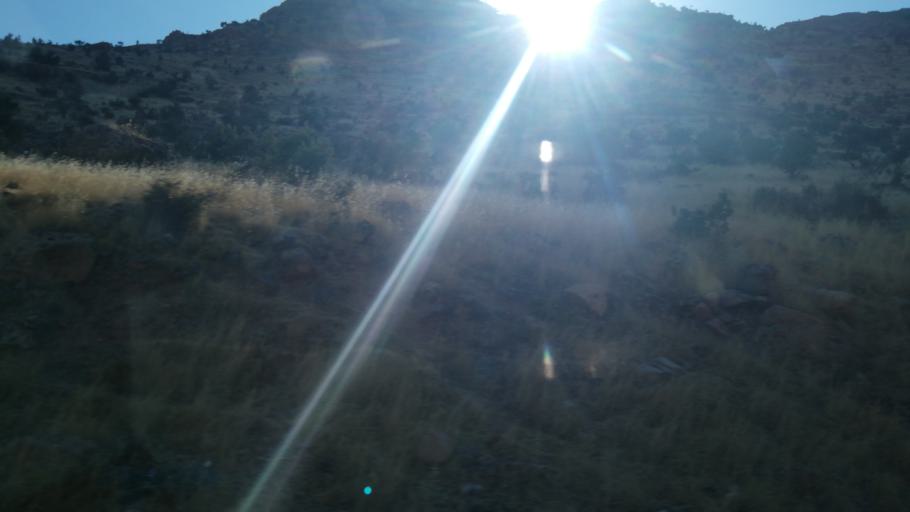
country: TR
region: Mardin
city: Sivrice
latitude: 37.2472
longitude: 41.3495
